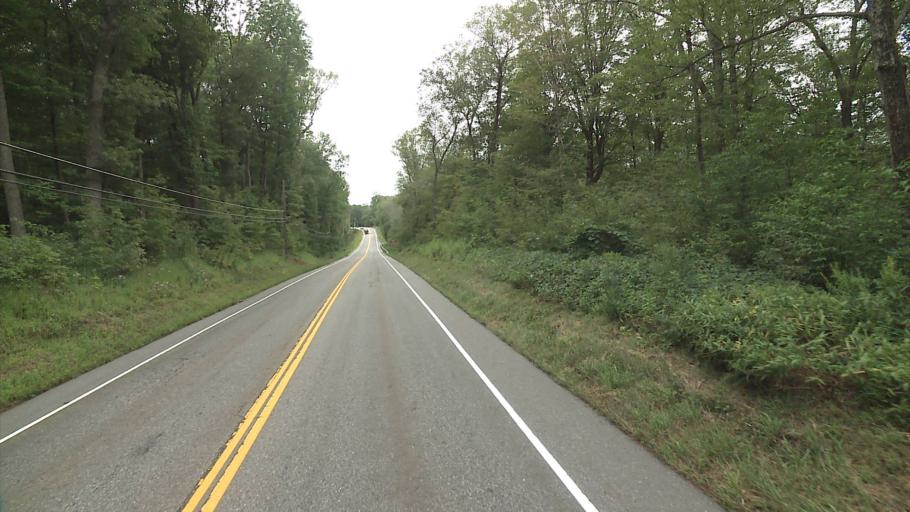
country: US
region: Connecticut
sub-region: Hartford County
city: Terramuggus
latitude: 41.7232
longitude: -72.4362
